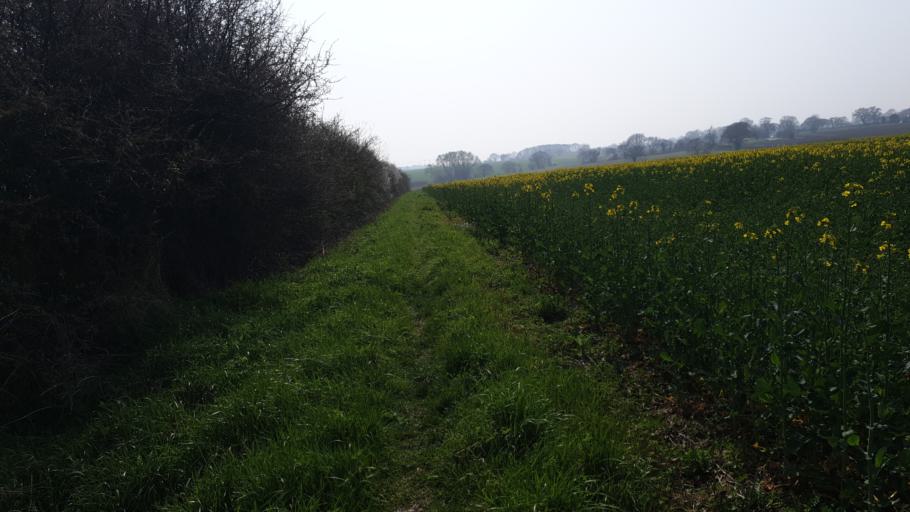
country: GB
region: England
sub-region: Essex
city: Mistley
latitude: 51.9368
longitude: 1.1712
